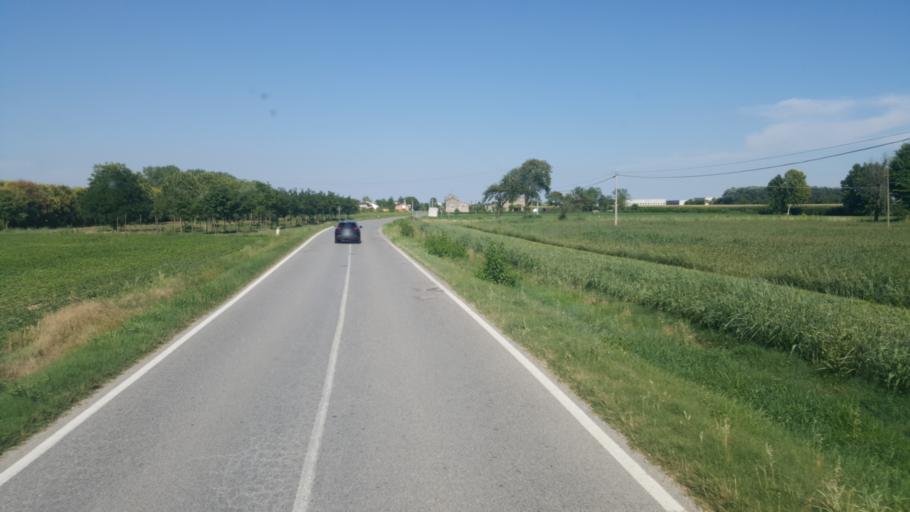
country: IT
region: Lombardy
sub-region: Provincia di Mantova
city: Casalromano
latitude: 45.1962
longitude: 10.3518
